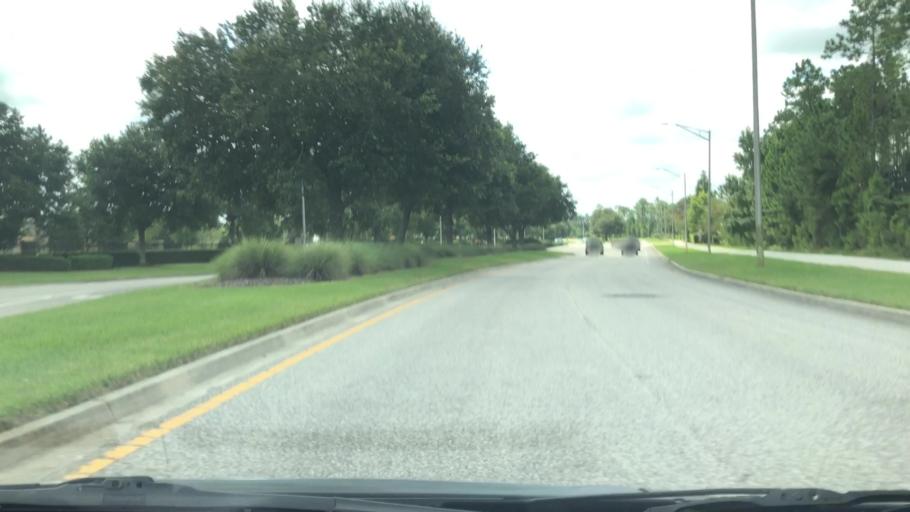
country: US
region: Florida
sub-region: Saint Johns County
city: Fruit Cove
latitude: 30.1345
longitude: -81.5445
